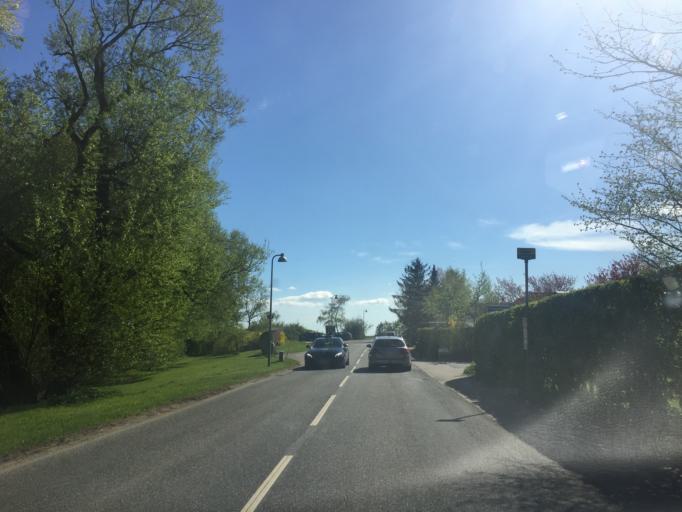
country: DK
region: Capital Region
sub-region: Egedal Kommune
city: Smorumnedre
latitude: 55.7136
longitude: 12.3096
